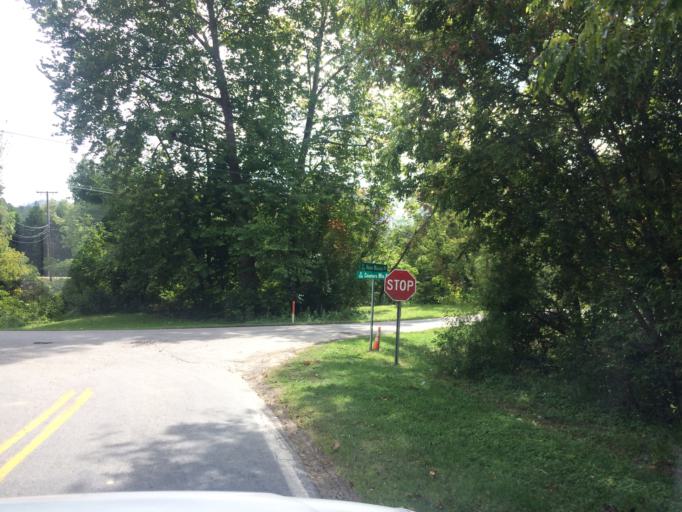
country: US
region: North Carolina
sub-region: Haywood County
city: Clyde
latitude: 35.5354
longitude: -82.9177
